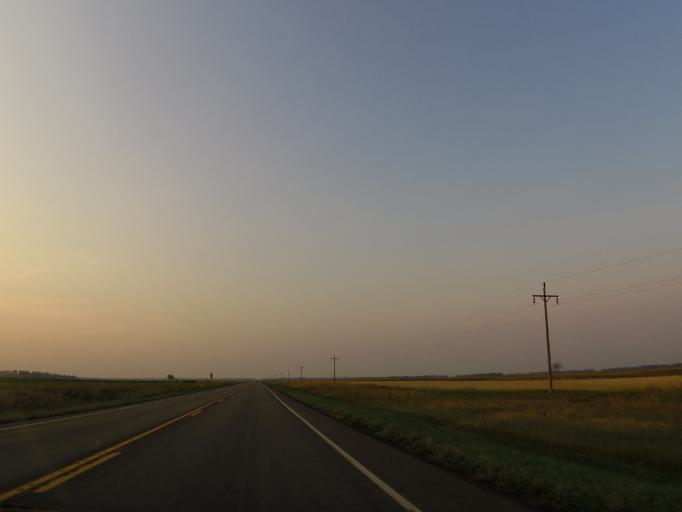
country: US
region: North Dakota
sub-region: Grand Forks County
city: Larimore
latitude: 48.0364
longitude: -97.6225
